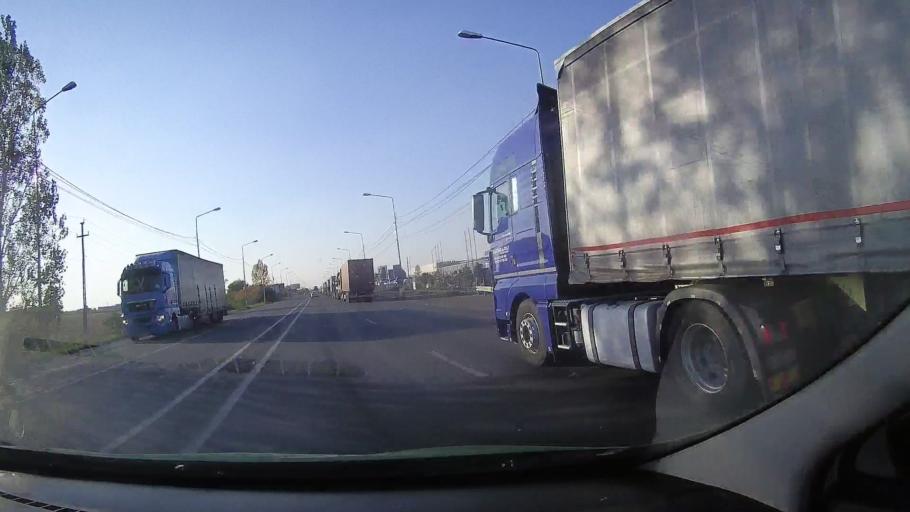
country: RO
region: Bihor
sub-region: Comuna Bors
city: Santion
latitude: 47.1029
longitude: 21.8373
